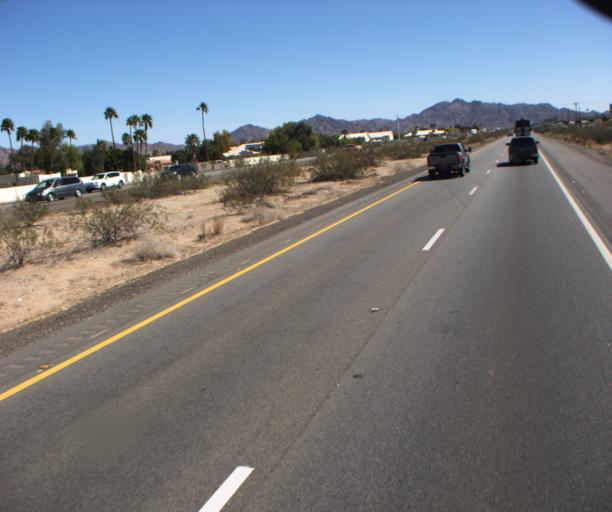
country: US
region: Arizona
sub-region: Yuma County
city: Fortuna Foothills
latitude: 32.6703
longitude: -114.4311
